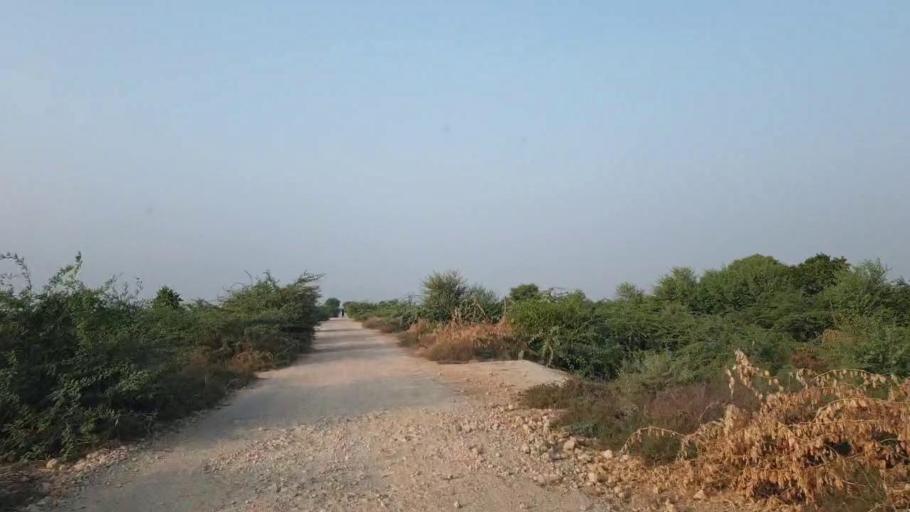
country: PK
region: Sindh
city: Rajo Khanani
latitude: 25.0272
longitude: 68.9772
